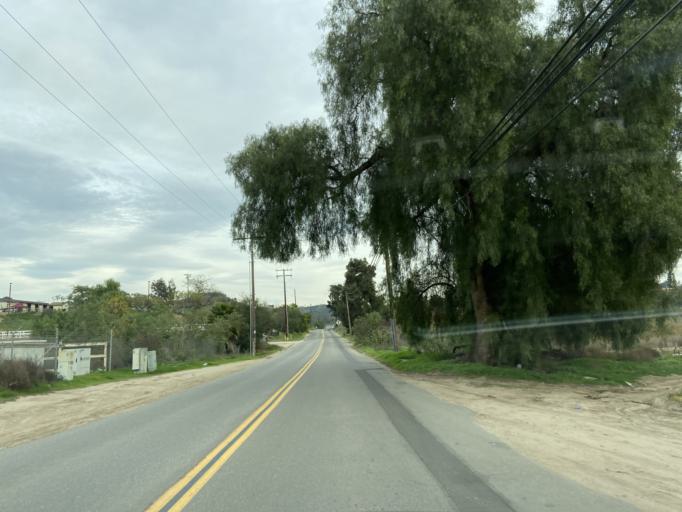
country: US
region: California
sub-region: San Diego County
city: Bonsall
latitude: 33.2682
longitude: -117.2402
